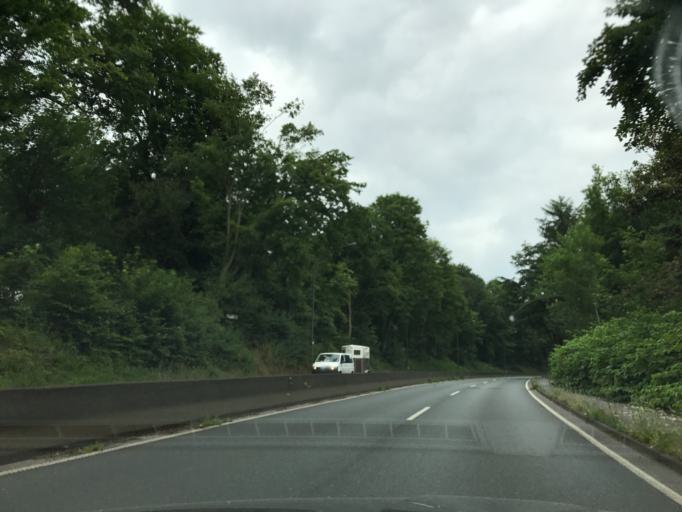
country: DE
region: North Rhine-Westphalia
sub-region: Regierungsbezirk Dusseldorf
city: Essen
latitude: 51.4044
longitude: 6.9893
